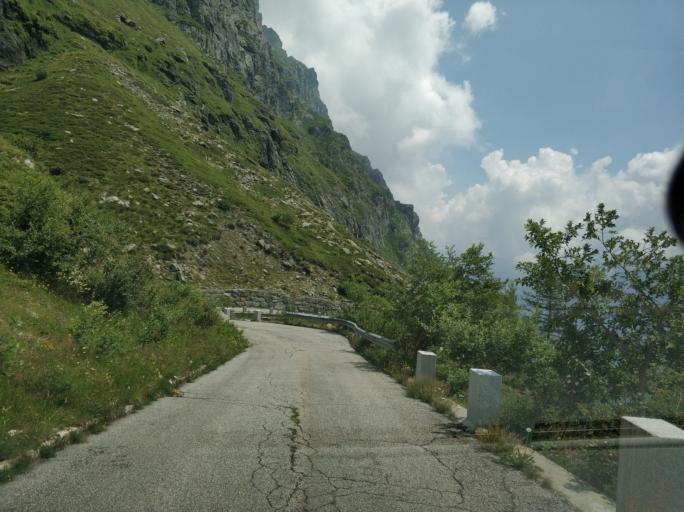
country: IT
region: Piedmont
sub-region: Provincia di Torino
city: Usseglio
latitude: 45.2504
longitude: 7.1809
